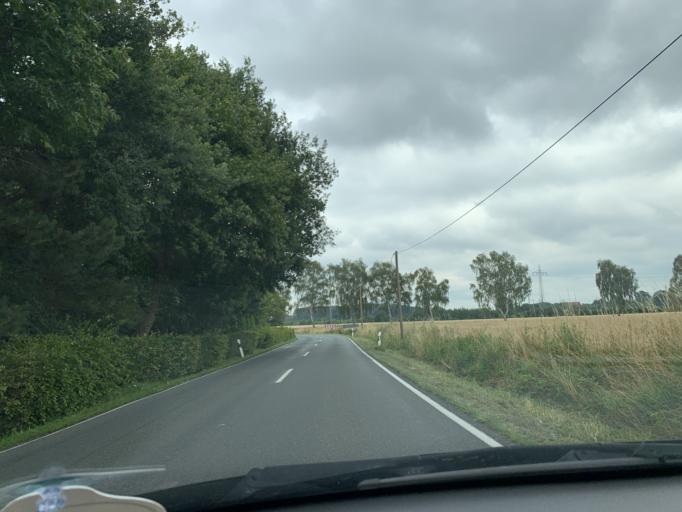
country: DE
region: North Rhine-Westphalia
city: Oelde
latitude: 51.8235
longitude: 8.0899
